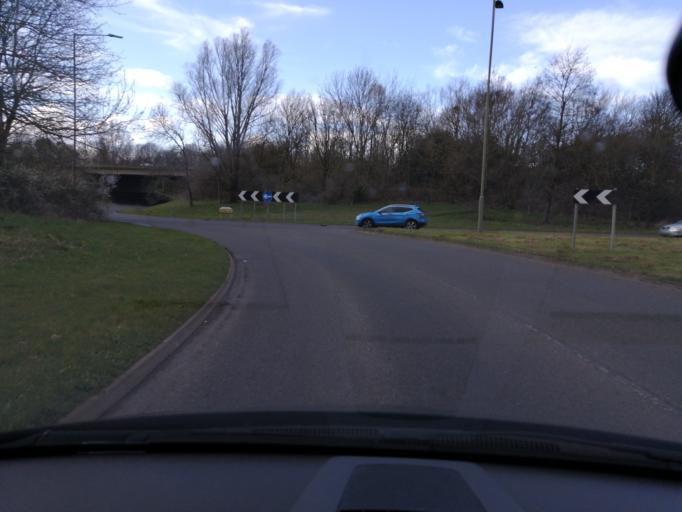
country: GB
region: England
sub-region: Peterborough
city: Peterborough
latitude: 52.5955
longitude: -0.2693
